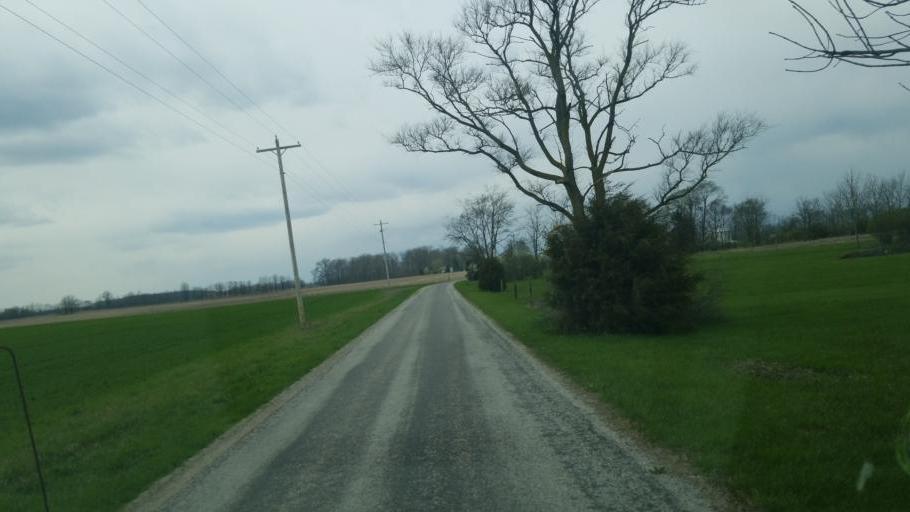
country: US
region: Ohio
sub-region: Marion County
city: Prospect
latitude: 40.3889
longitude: -83.2050
